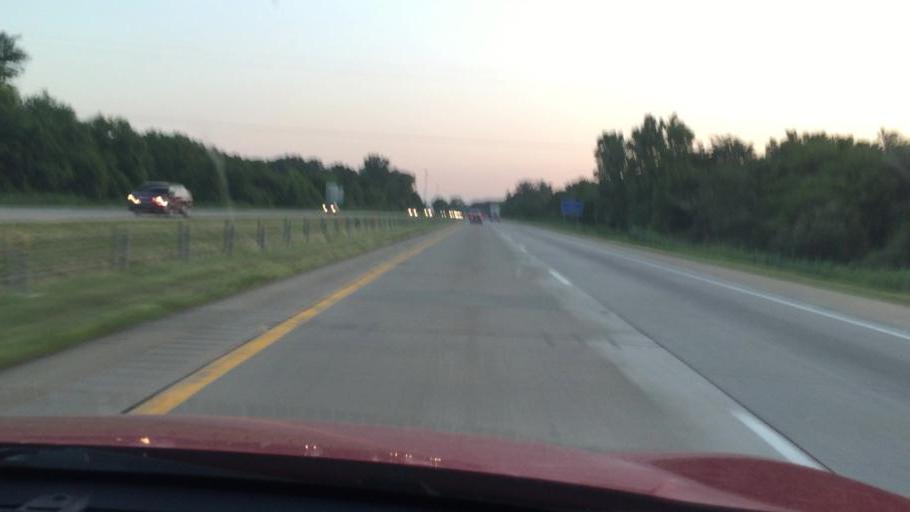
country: US
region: Michigan
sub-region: Monroe County
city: Lambertville
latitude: 41.8123
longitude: -83.6838
